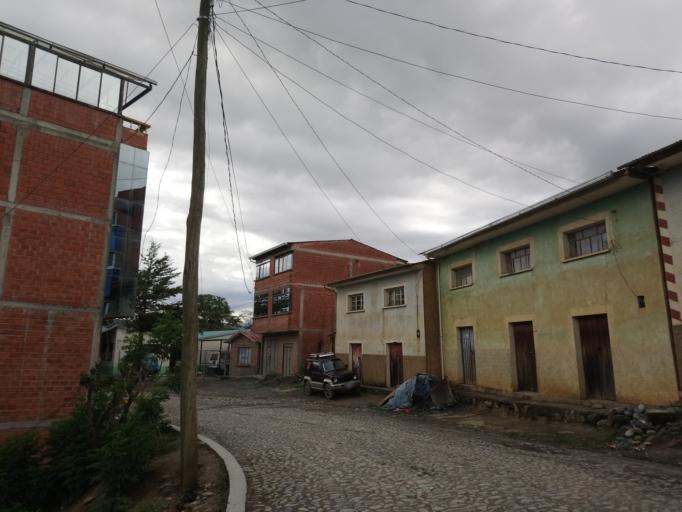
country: BO
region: La Paz
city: Coripata
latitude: -16.2702
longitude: -67.6387
